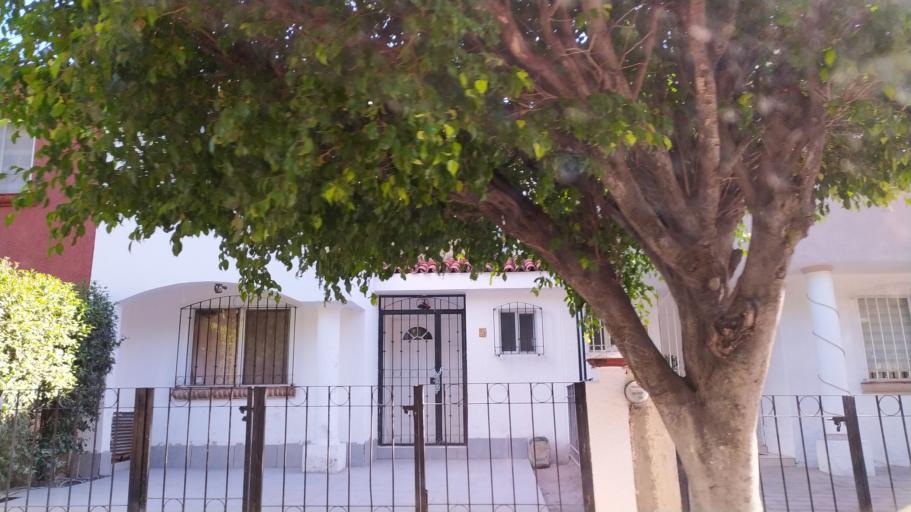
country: MX
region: Jalisco
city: Guadalajara
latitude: 20.6561
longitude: -103.4336
